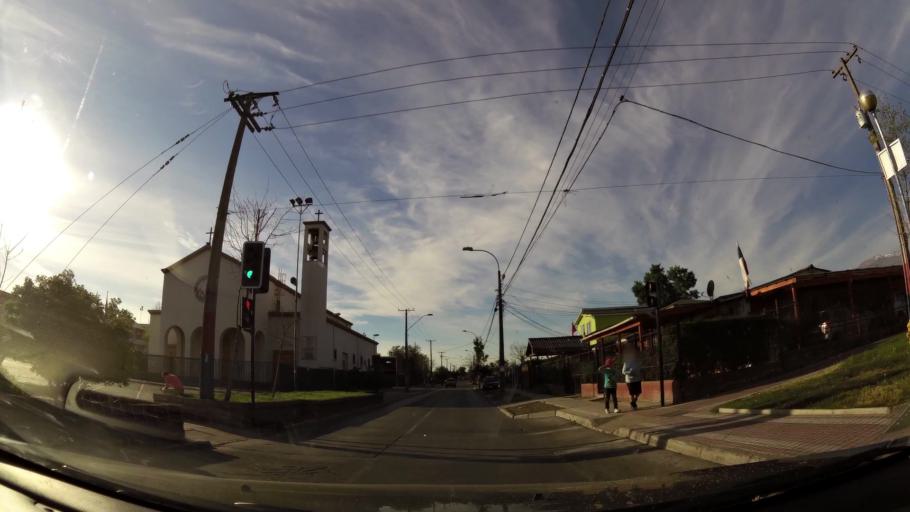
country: CL
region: Santiago Metropolitan
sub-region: Provincia de Cordillera
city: Puente Alto
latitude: -33.6167
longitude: -70.5780
